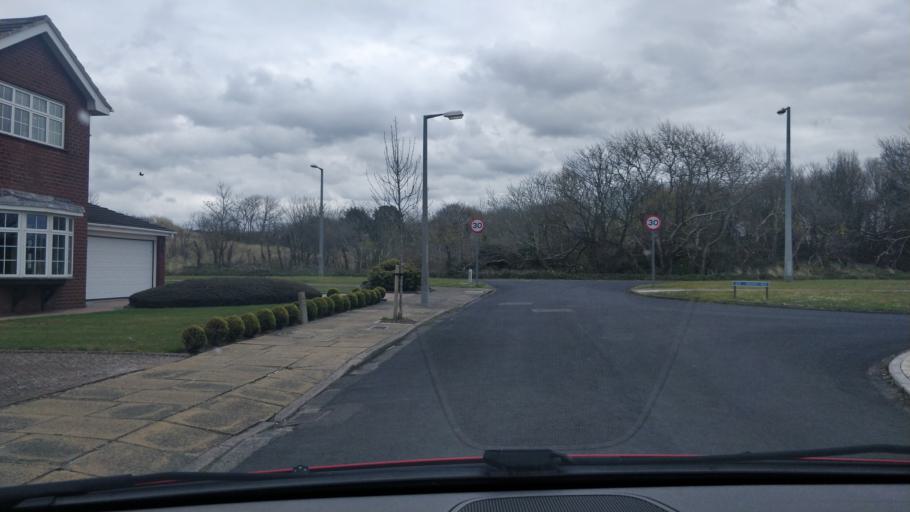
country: GB
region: England
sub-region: Sefton
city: Formby
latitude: 53.6020
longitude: -3.0506
